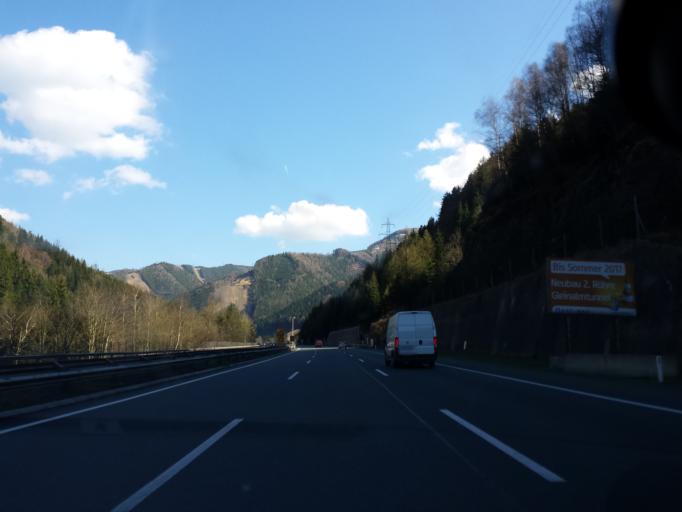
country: AT
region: Styria
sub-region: Politischer Bezirk Leoben
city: Sankt Michael in Obersteiermark
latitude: 47.3047
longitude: 15.0621
